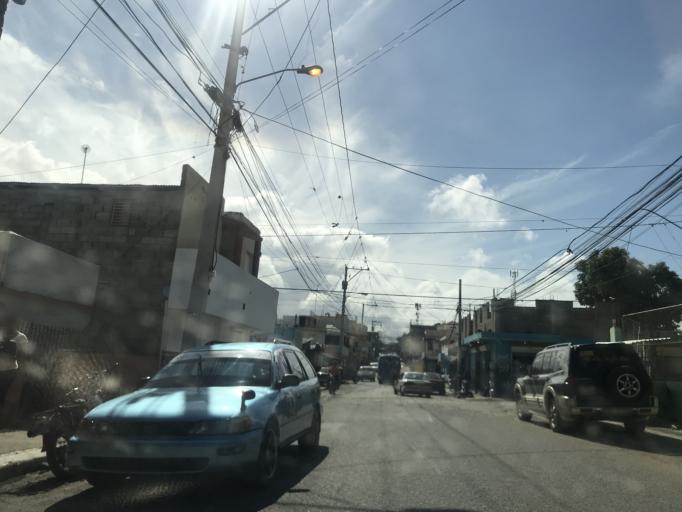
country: DO
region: Santiago
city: Palmar Arriba
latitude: 19.4852
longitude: -70.7457
